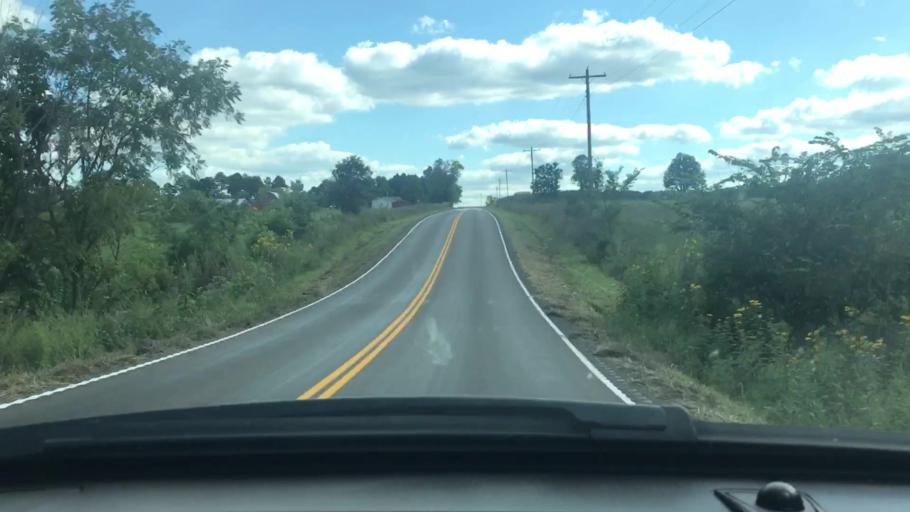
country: US
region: Missouri
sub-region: Wright County
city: Mountain Grove
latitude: 37.2389
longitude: -92.3005
